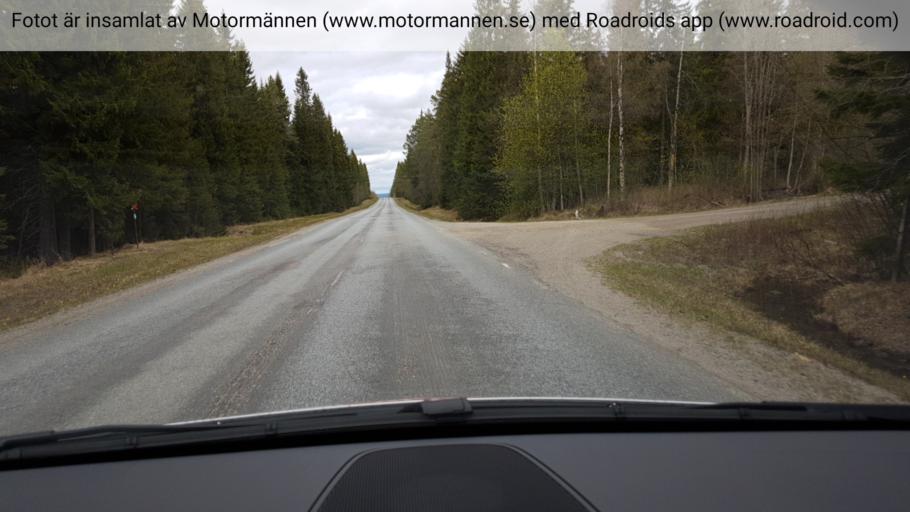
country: SE
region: Jaemtland
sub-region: Braecke Kommun
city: Braecke
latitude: 62.8017
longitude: 15.4665
